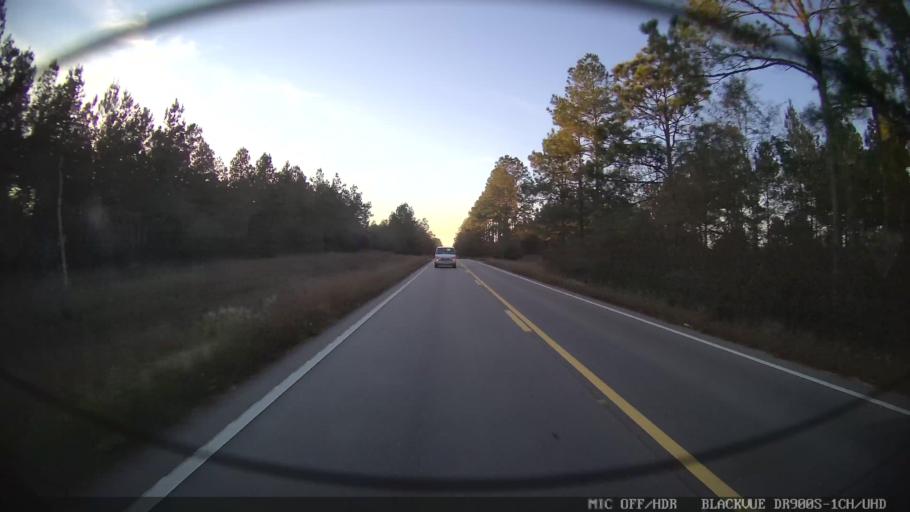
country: US
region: Mississippi
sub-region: Lamar County
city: Lumberton
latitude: 30.9961
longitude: -89.2934
